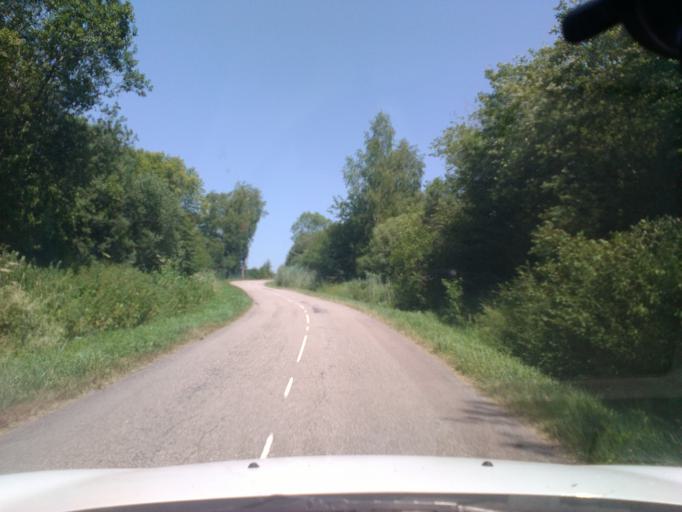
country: FR
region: Lorraine
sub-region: Departement des Vosges
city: Liffol-le-Grand
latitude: 48.3593
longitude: 5.6152
